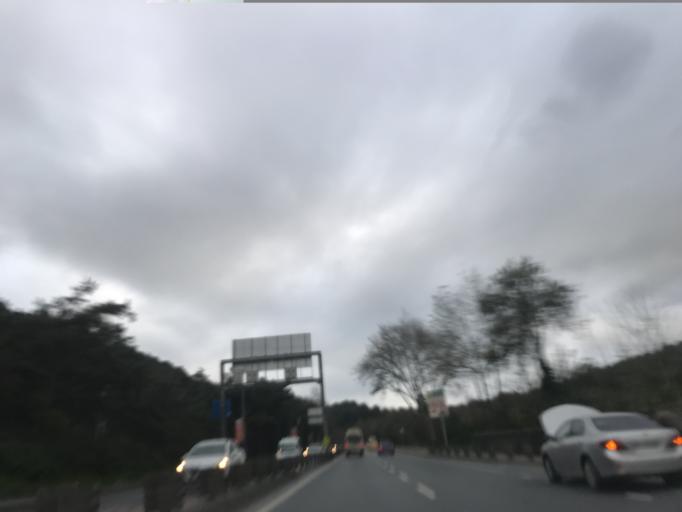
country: TR
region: Istanbul
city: Arikoey
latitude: 41.1499
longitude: 29.0294
